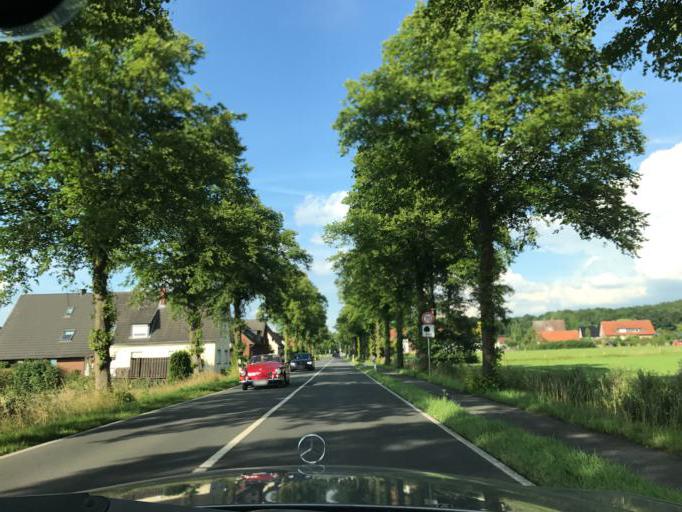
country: DE
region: Lower Saxony
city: Hasbergen
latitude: 52.2164
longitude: 7.9335
